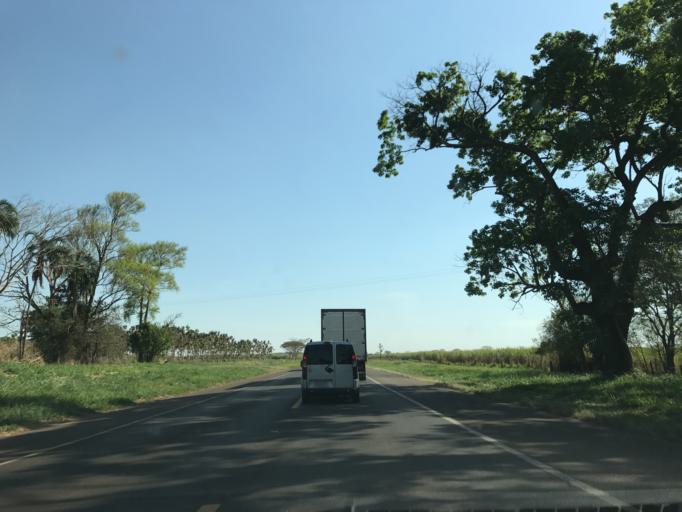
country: BR
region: Sao Paulo
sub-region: Penapolis
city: Penapolis
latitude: -21.4793
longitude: -50.2013
